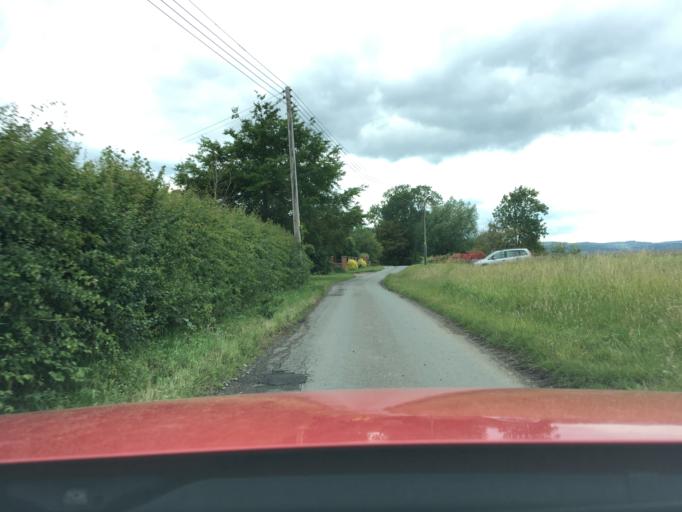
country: GB
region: England
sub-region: Gloucestershire
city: Stonehouse
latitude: 51.7923
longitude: -2.3737
